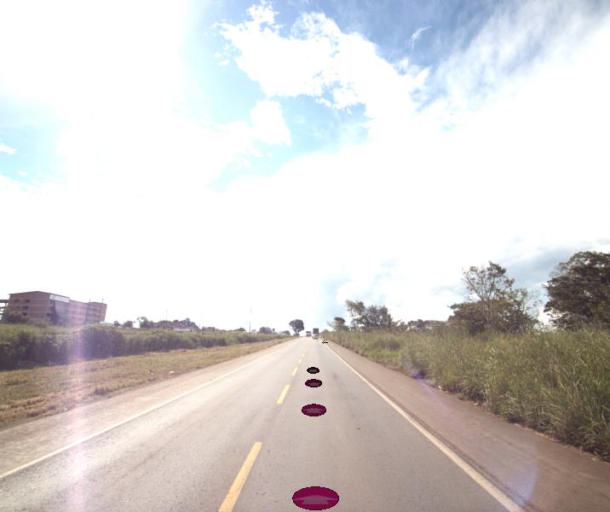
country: BR
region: Goias
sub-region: Jaragua
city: Jaragua
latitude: -15.7449
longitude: -49.3192
